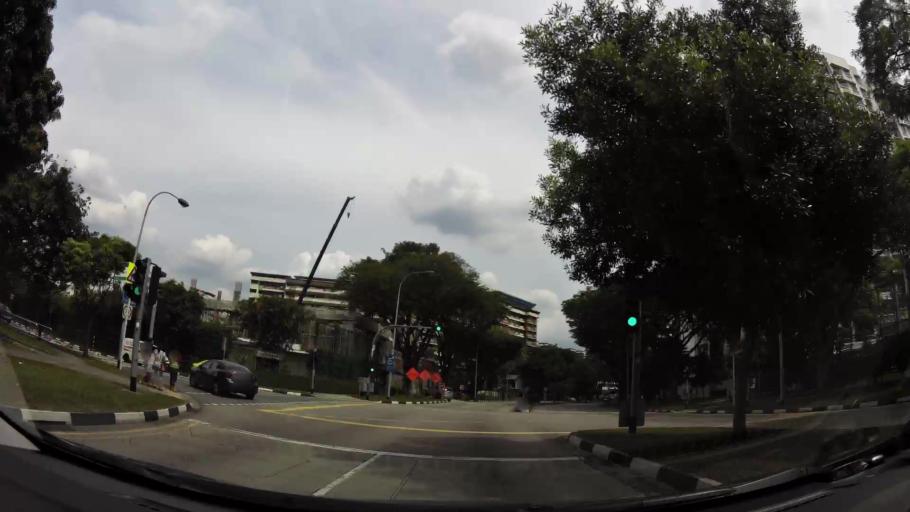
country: MY
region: Johor
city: Johor Bahru
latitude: 1.4322
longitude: 103.7894
